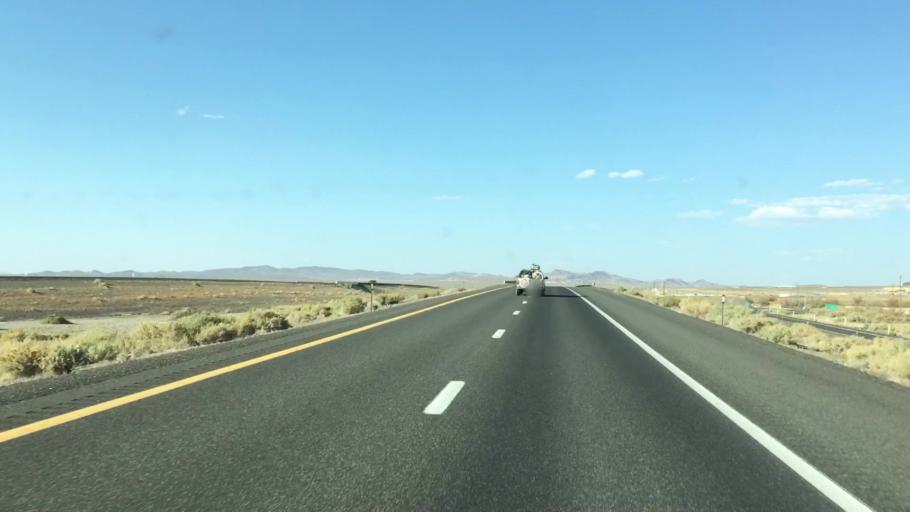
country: US
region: Nevada
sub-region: Lyon County
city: Fernley
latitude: 39.7887
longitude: -119.0224
